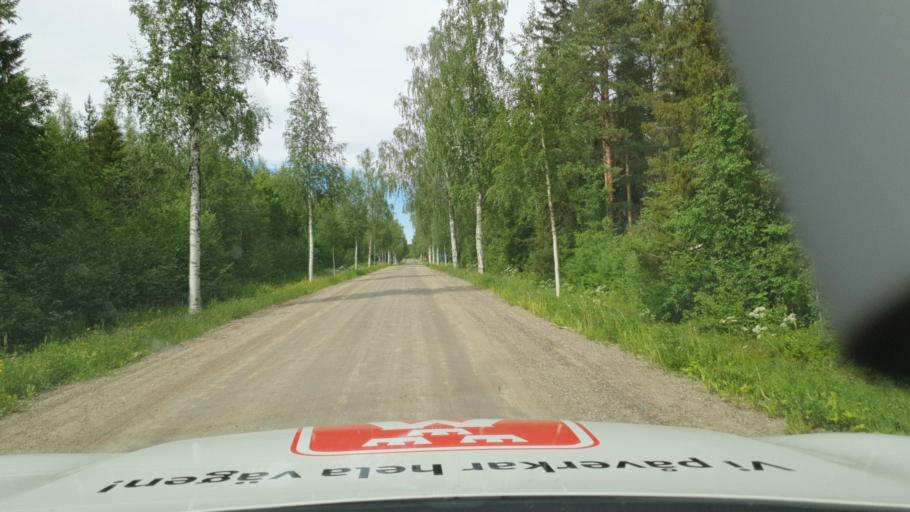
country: SE
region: Vaesterbotten
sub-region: Skelleftea Kommun
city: Burtraesk
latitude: 64.4624
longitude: 20.4666
